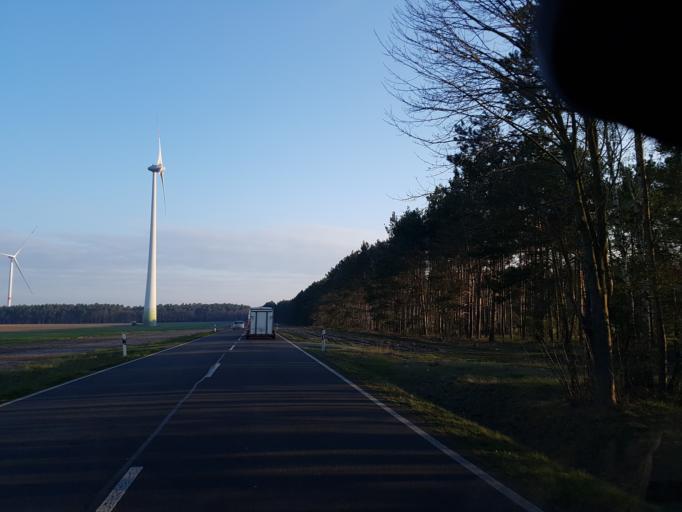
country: DE
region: Saxony-Anhalt
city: Holzdorf
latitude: 51.8527
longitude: 13.1473
